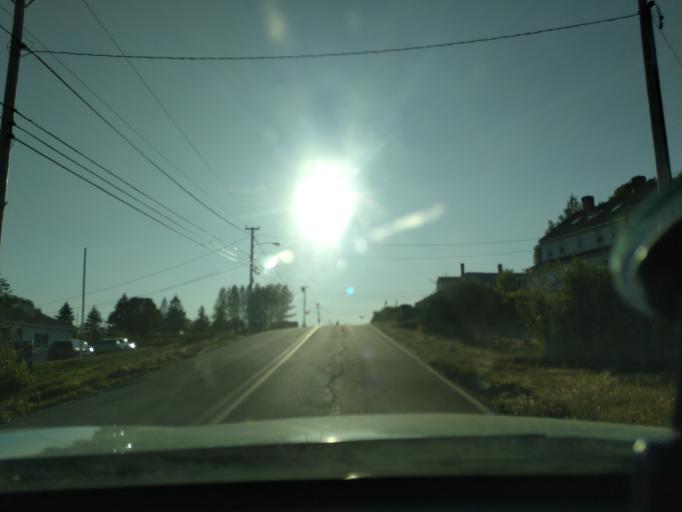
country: US
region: Maine
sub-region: Washington County
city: Machiasport
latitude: 44.6580
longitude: -67.2095
